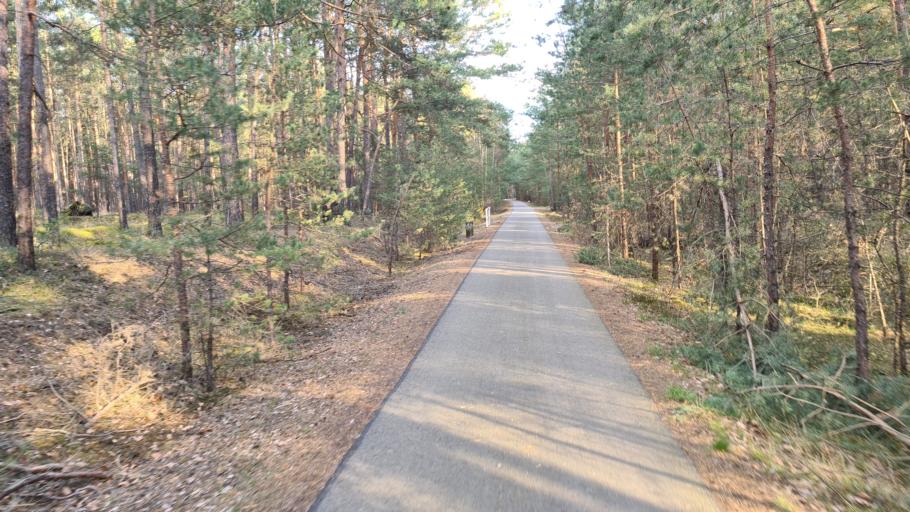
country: DE
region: Brandenburg
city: Schonborn
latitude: 51.5566
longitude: 13.5068
